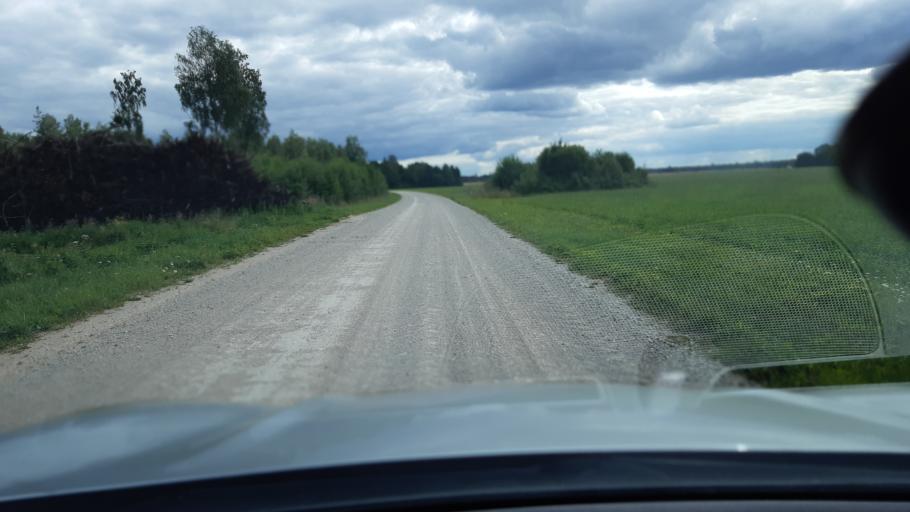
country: EE
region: Paernumaa
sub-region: Vaendra vald (alev)
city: Vandra
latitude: 58.7865
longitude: 25.0269
